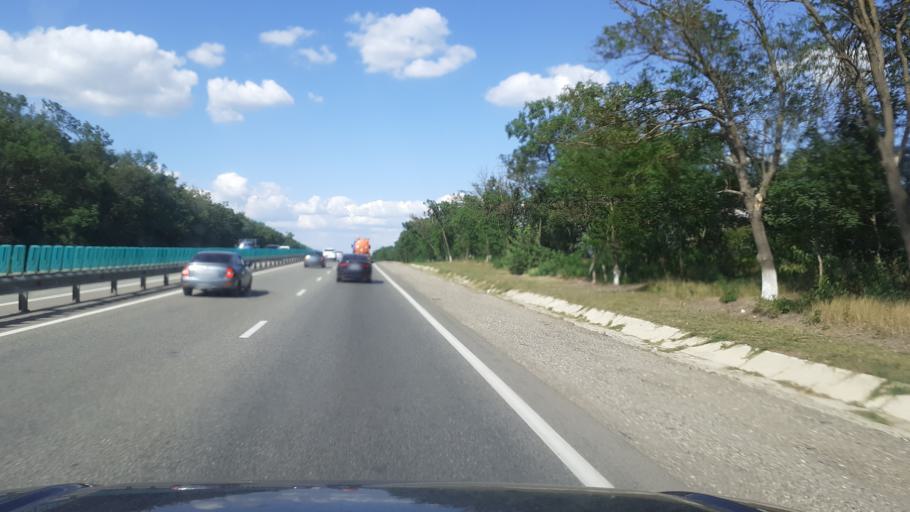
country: RU
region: Krasnodarskiy
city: Severskaya
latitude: 44.8470
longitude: 38.7024
